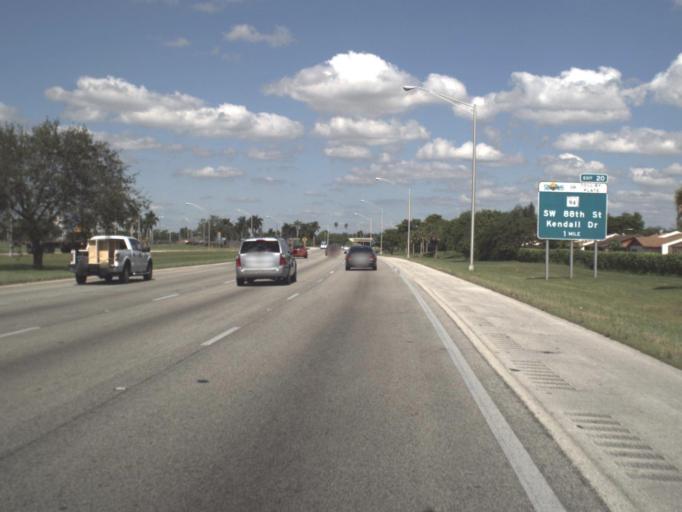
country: US
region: Florida
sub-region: Miami-Dade County
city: The Crossings
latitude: 25.6648
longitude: -80.3863
